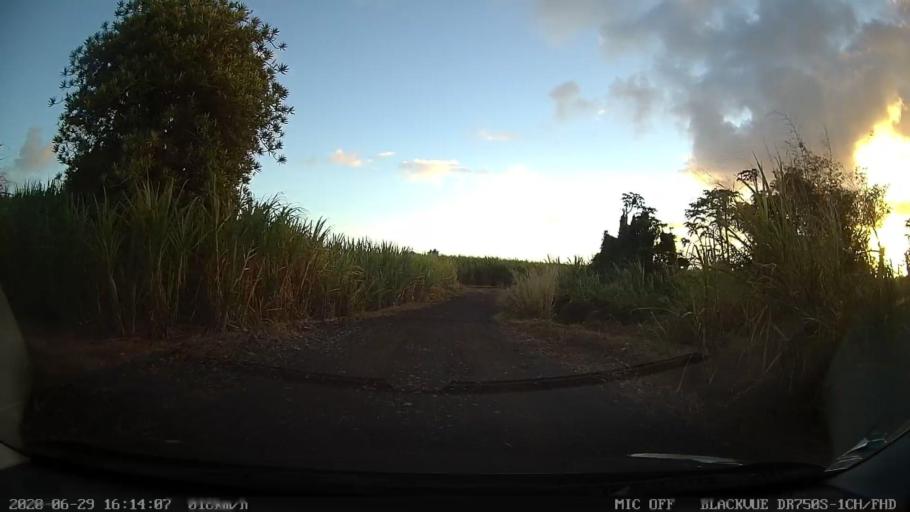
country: RE
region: Reunion
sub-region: Reunion
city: Bras-Panon
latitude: -20.9897
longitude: 55.6965
